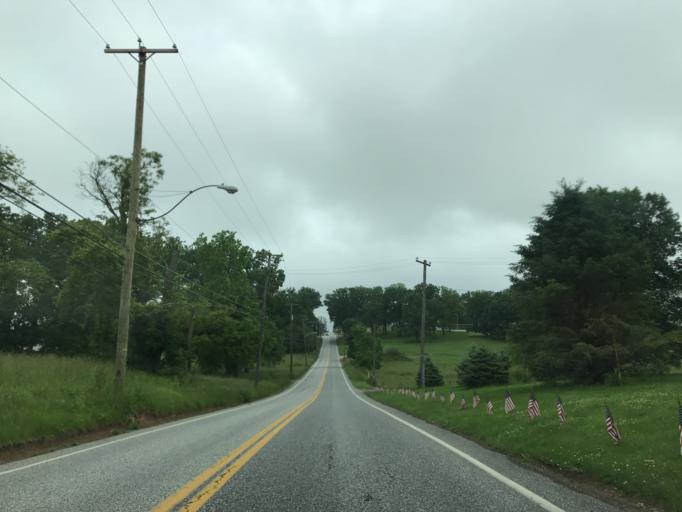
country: US
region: Pennsylvania
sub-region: York County
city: Susquehanna Trails
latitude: 39.7337
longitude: -76.4516
